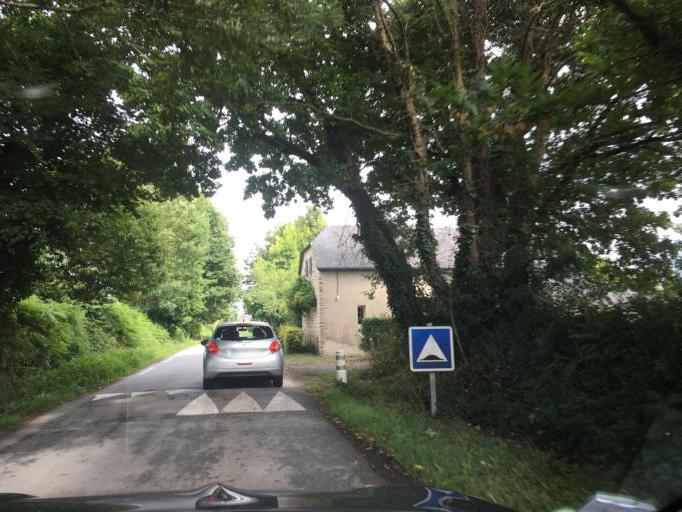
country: FR
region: Aquitaine
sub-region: Departement des Pyrenees-Atlantiques
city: Ousse
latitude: 43.3137
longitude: -0.2858
